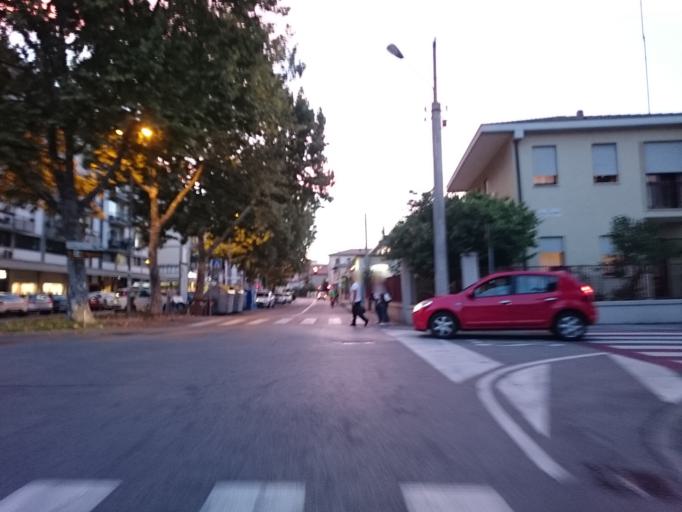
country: IT
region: Veneto
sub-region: Provincia di Padova
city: Padova
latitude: 45.3895
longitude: 11.8916
